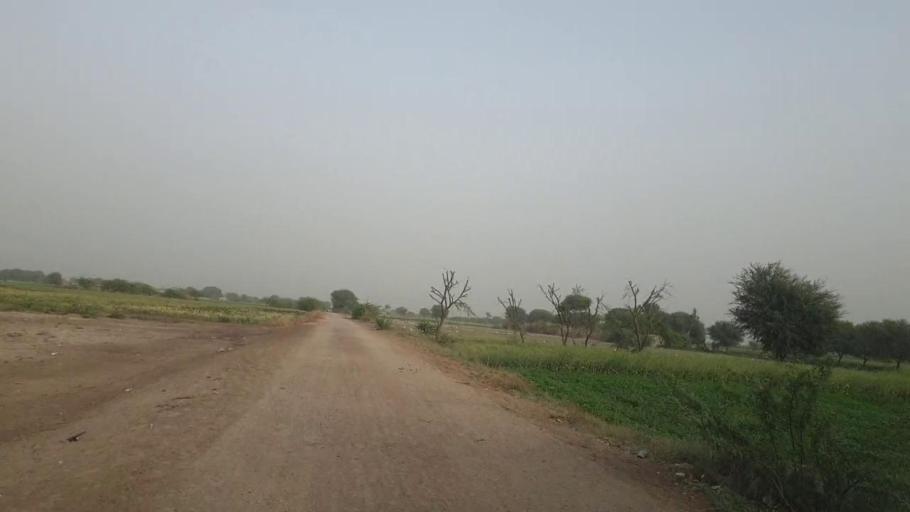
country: PK
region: Sindh
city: Kunri
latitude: 25.0968
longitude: 69.4417
